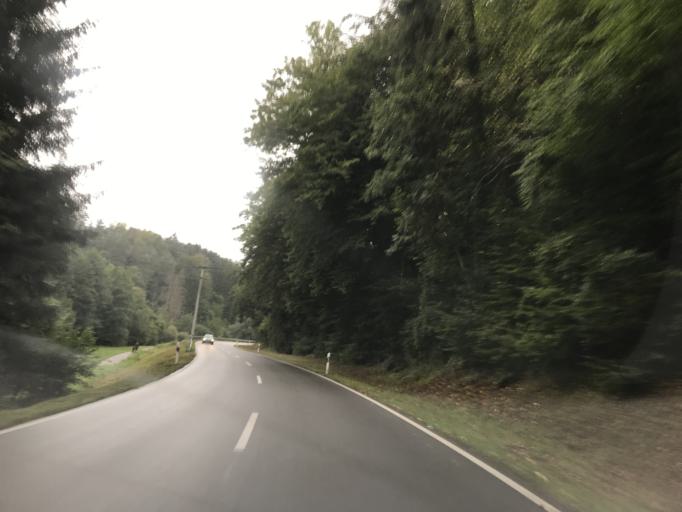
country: DE
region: Baden-Wuerttemberg
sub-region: Freiburg Region
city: Schworstadt
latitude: 47.5968
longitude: 7.8672
